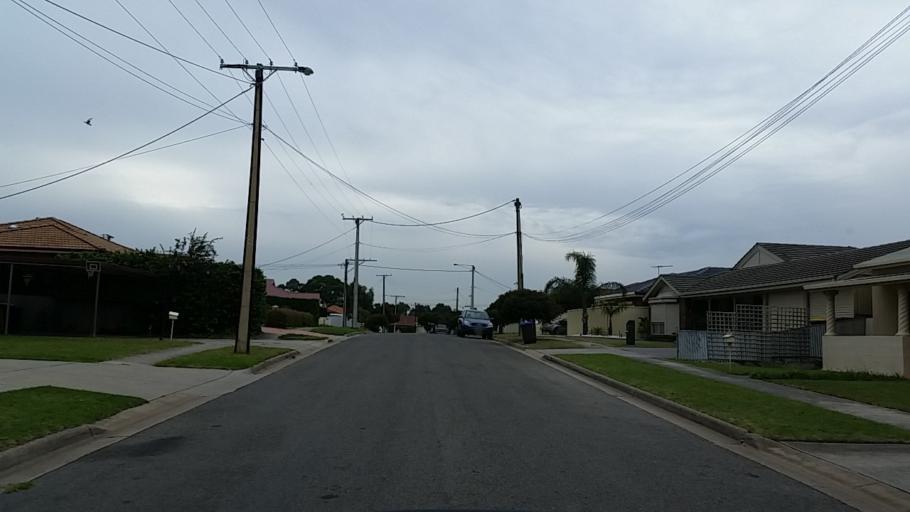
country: AU
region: South Australia
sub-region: Charles Sturt
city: Royal Park
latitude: -34.8762
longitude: 138.5063
